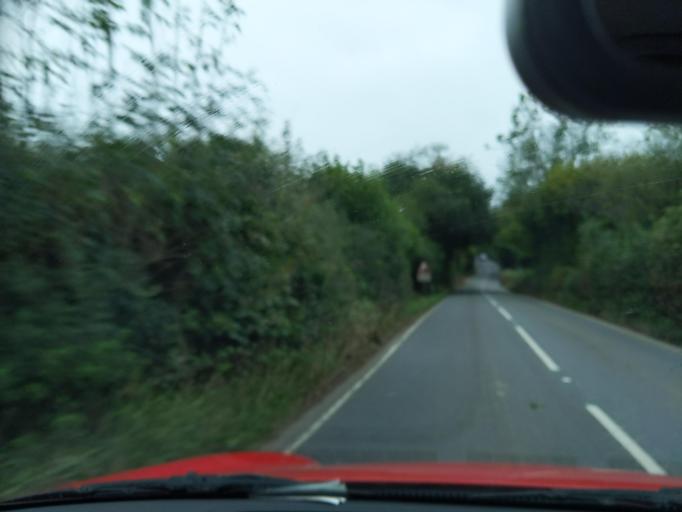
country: GB
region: England
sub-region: Devon
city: Okehampton
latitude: 50.8385
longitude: -4.0753
